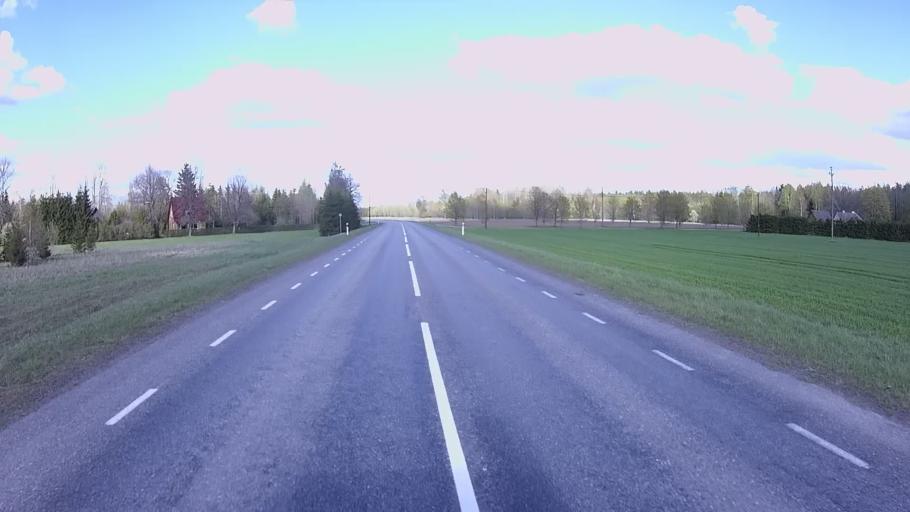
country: EE
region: Jogevamaa
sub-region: Poltsamaa linn
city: Poltsamaa
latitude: 58.7016
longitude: 26.1500
